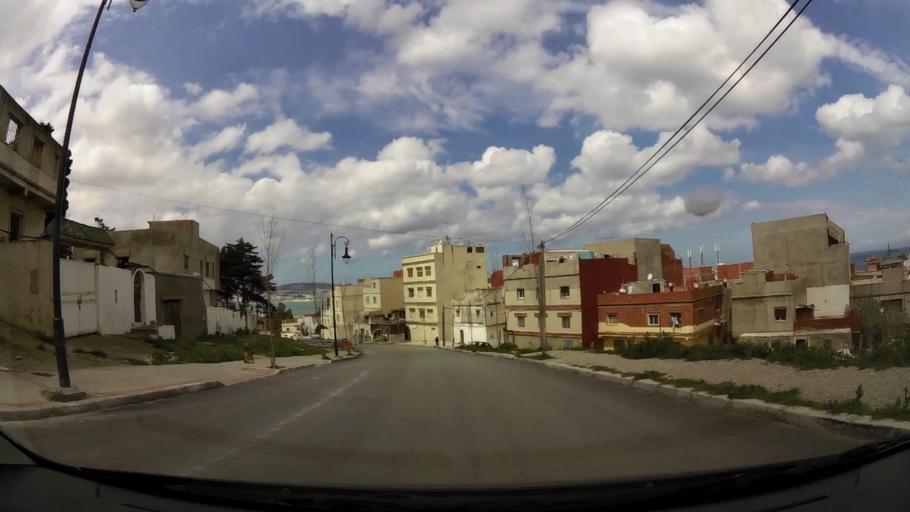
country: MA
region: Tanger-Tetouan
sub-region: Tanger-Assilah
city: Tangier
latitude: 35.7793
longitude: -5.7546
